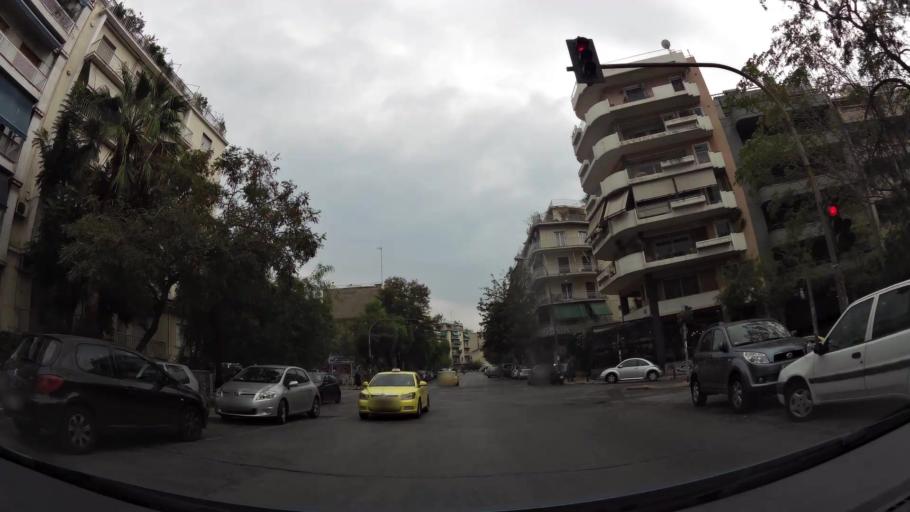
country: GR
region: Attica
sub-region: Nomarchia Athinas
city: Vyronas
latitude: 37.9728
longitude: 23.7469
